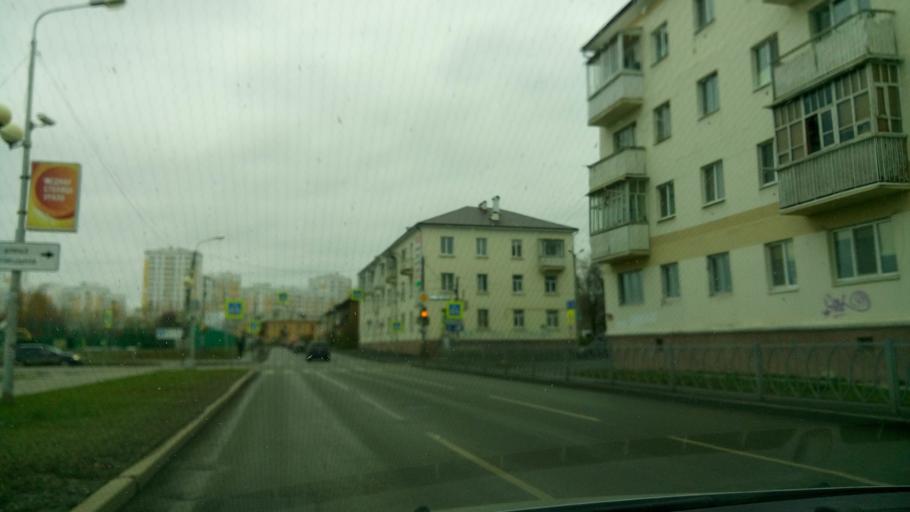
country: RU
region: Sverdlovsk
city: Verkhnyaya Pyshma
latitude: 56.9687
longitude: 60.5799
